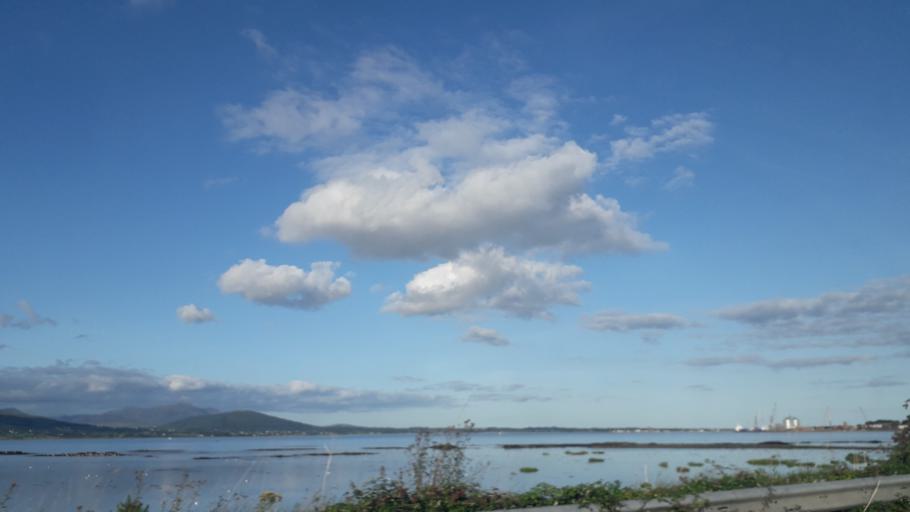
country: IE
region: Leinster
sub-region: Lu
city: Carlingford
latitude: 54.0334
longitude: -6.1618
